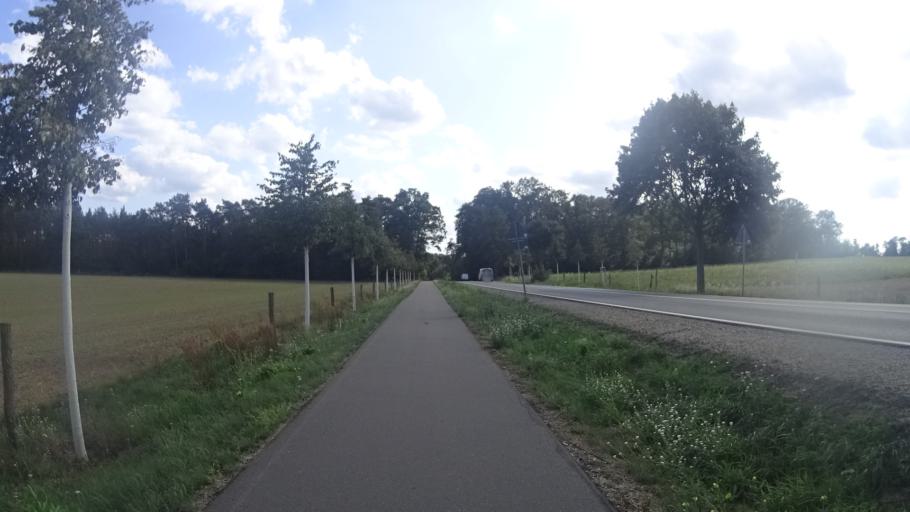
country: DE
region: Brandenburg
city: Rhinow
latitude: 52.6912
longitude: 12.3650
